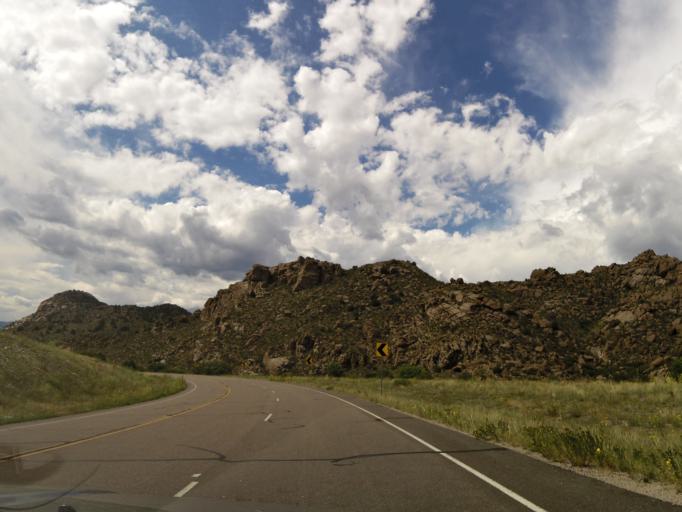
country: US
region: Colorado
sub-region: Custer County
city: Westcliffe
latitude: 38.3964
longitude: -105.6306
